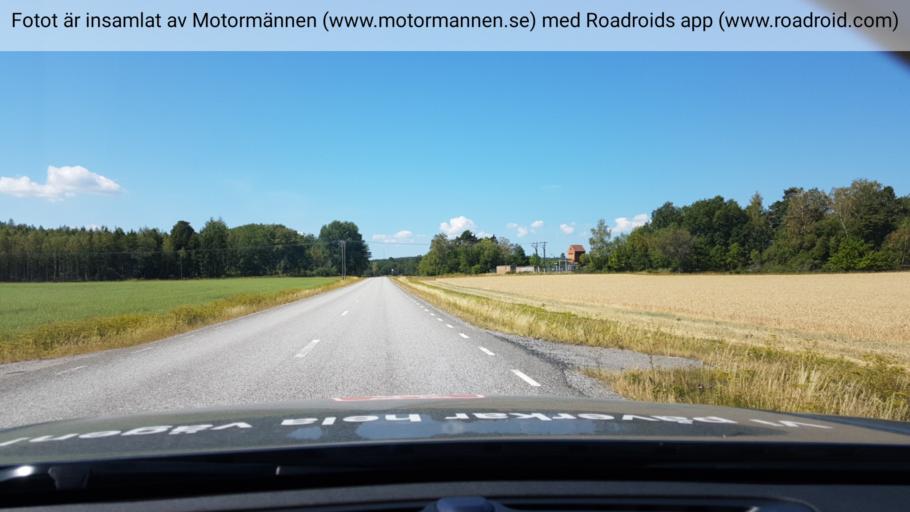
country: SE
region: Stockholm
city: Stenhamra
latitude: 59.3970
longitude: 17.5484
